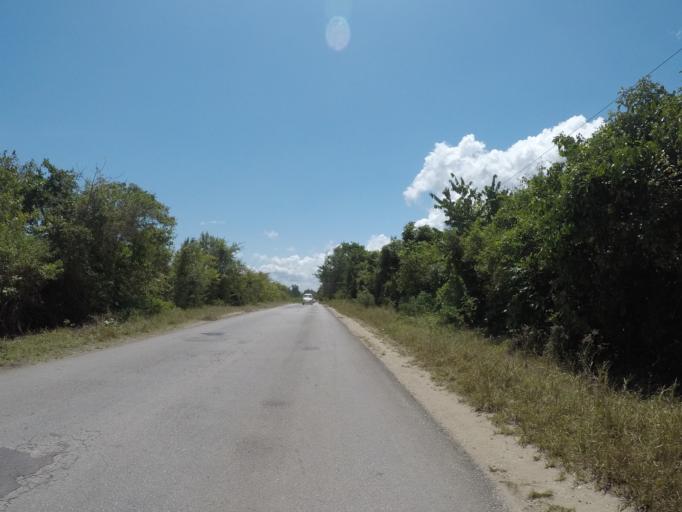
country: TZ
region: Zanzibar Central/South
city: Nganane
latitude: -6.2764
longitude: 39.4314
